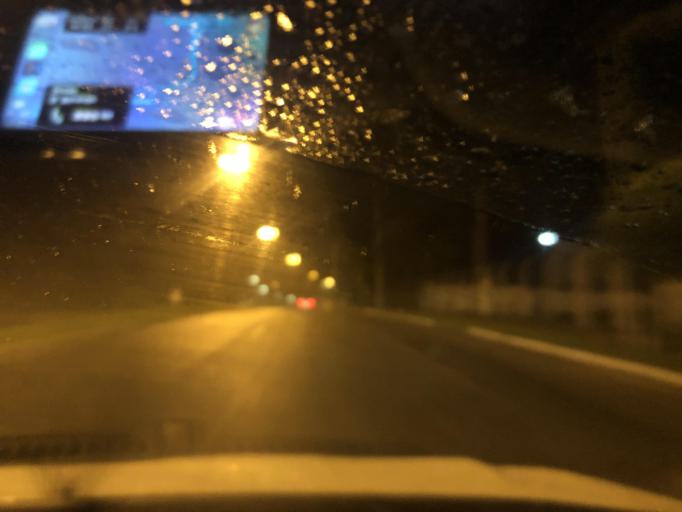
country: BR
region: Santa Catarina
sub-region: Joinville
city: Joinville
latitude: -26.3750
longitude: -48.8373
